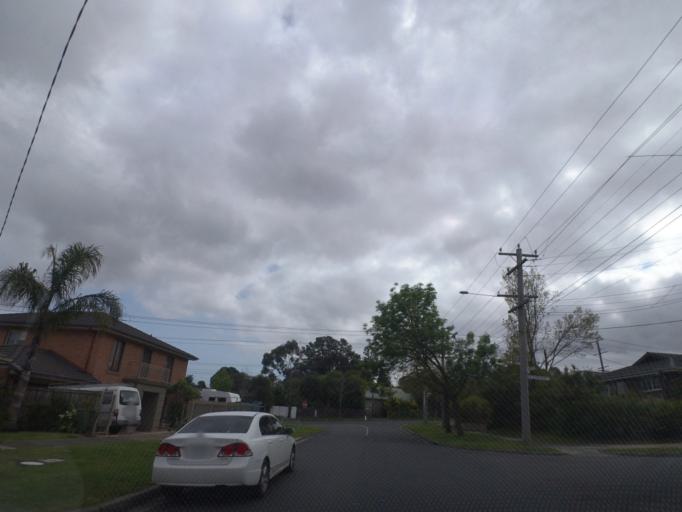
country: AU
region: Victoria
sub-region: Whitehorse
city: Nunawading
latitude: -37.8100
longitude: 145.1846
